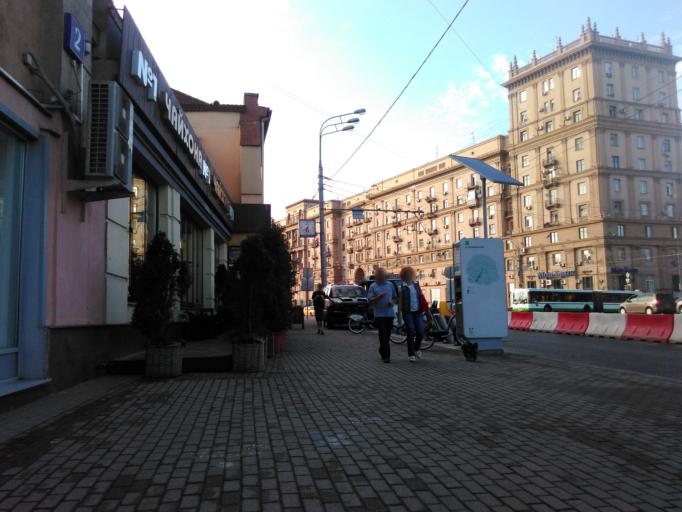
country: RU
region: Moscow
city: Taganskiy
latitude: 55.7635
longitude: 37.6563
